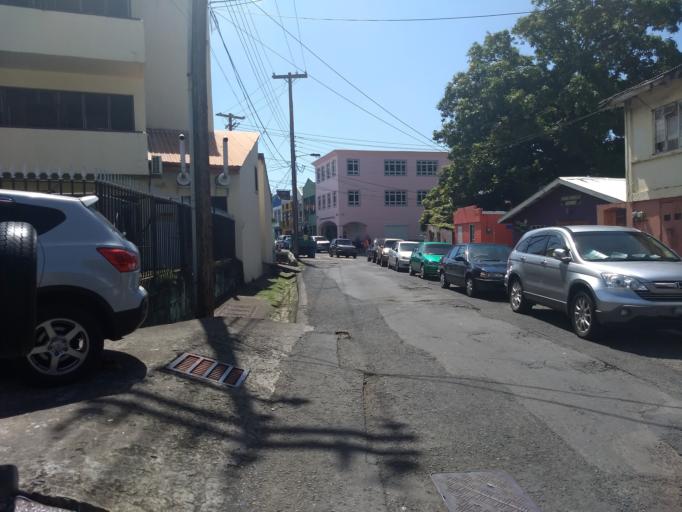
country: VC
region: Saint George
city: Kingstown Park
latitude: 13.1582
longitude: -61.2310
